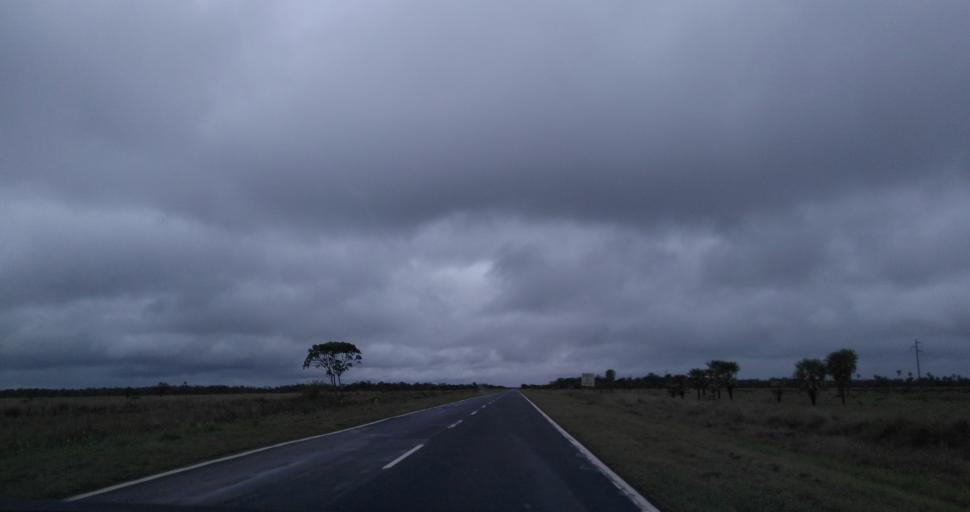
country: AR
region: Formosa
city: Clorinda
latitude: -25.6245
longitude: -57.9151
